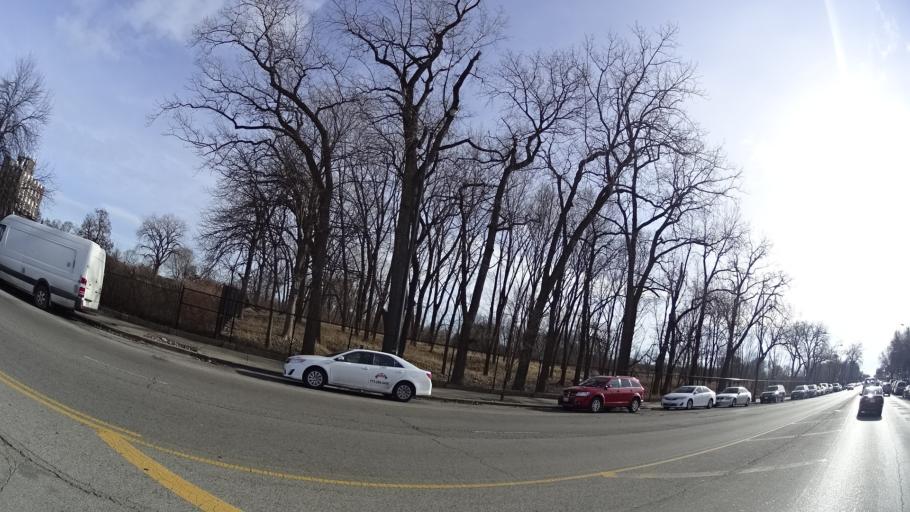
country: US
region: Illinois
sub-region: Cook County
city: Lincolnwood
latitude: 41.9900
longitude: -87.6897
